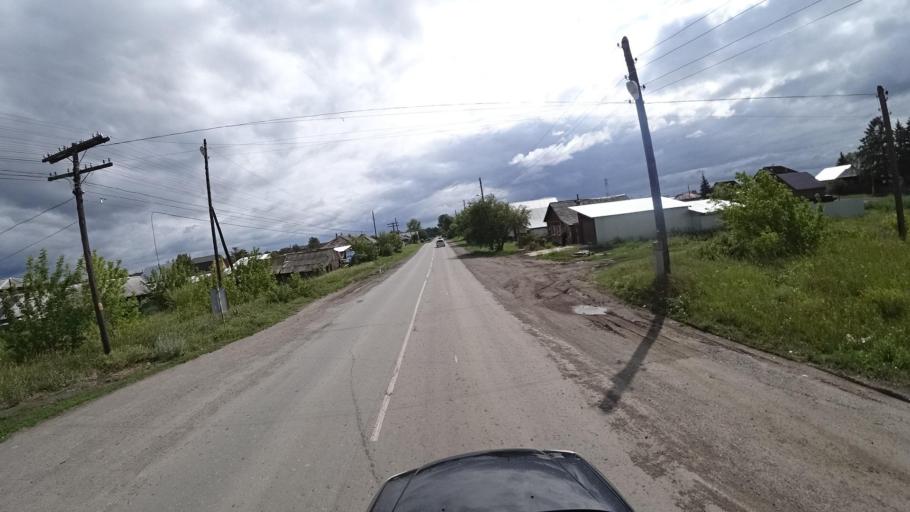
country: RU
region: Sverdlovsk
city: Kamyshlov
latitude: 56.8638
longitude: 62.7096
